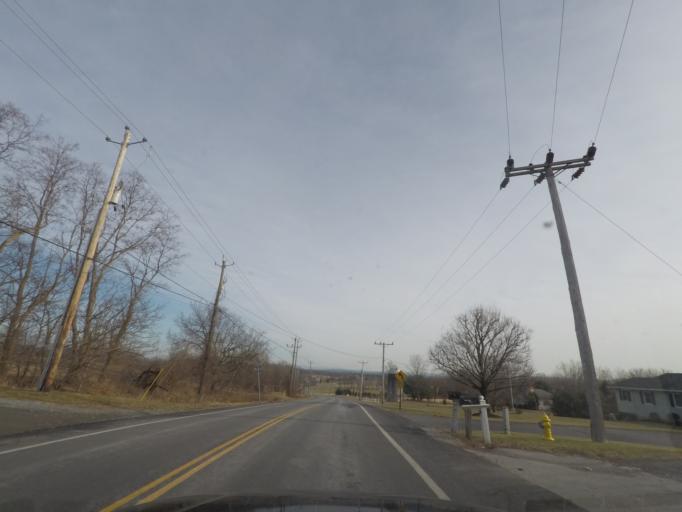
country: US
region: New York
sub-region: Saratoga County
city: Mechanicville
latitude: 42.8716
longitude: -73.7233
